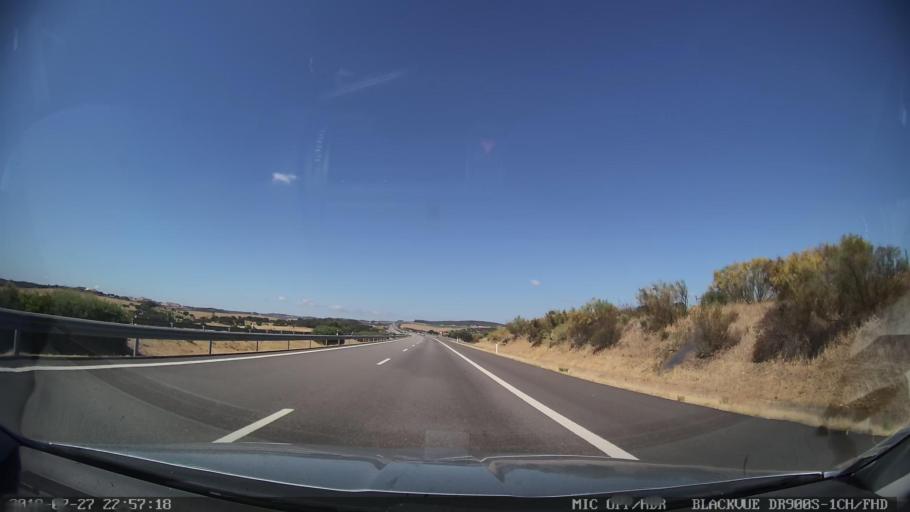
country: PT
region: Evora
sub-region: Borba
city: Borba
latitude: 38.8339
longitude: -7.4147
